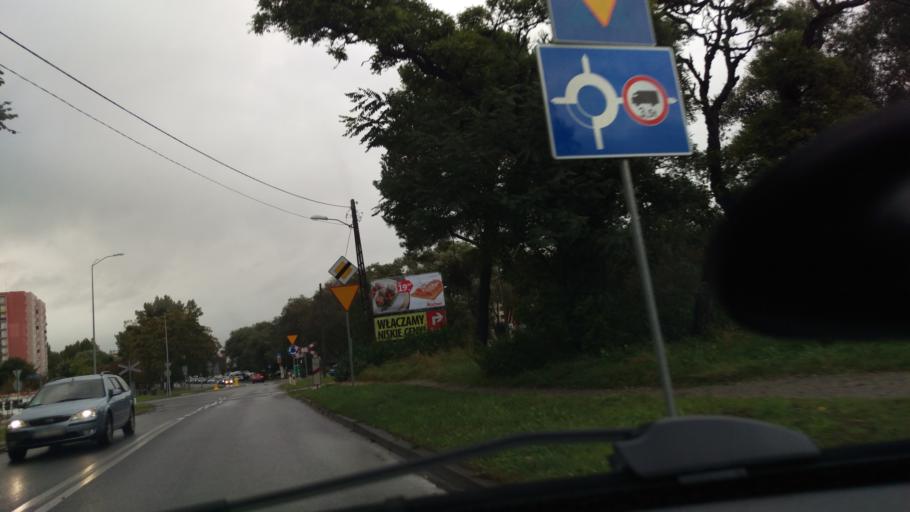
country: PL
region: West Pomeranian Voivodeship
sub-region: Szczecin
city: Szczecin
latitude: 53.3728
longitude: 14.6608
